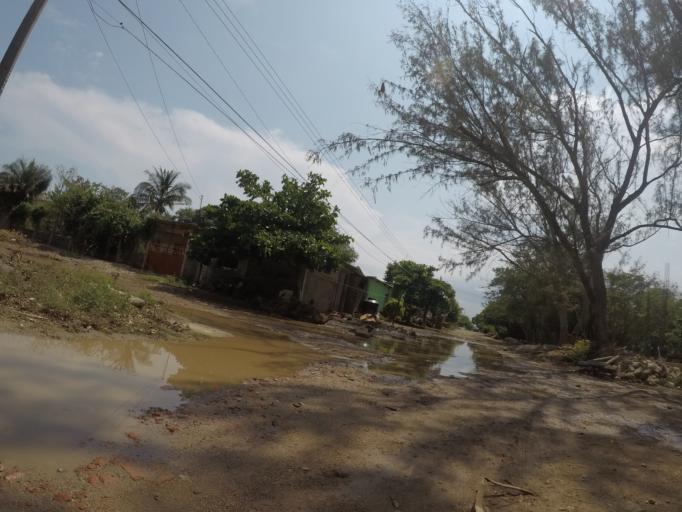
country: MX
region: Oaxaca
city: Union Hidalgo
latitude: 16.4655
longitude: -94.8314
